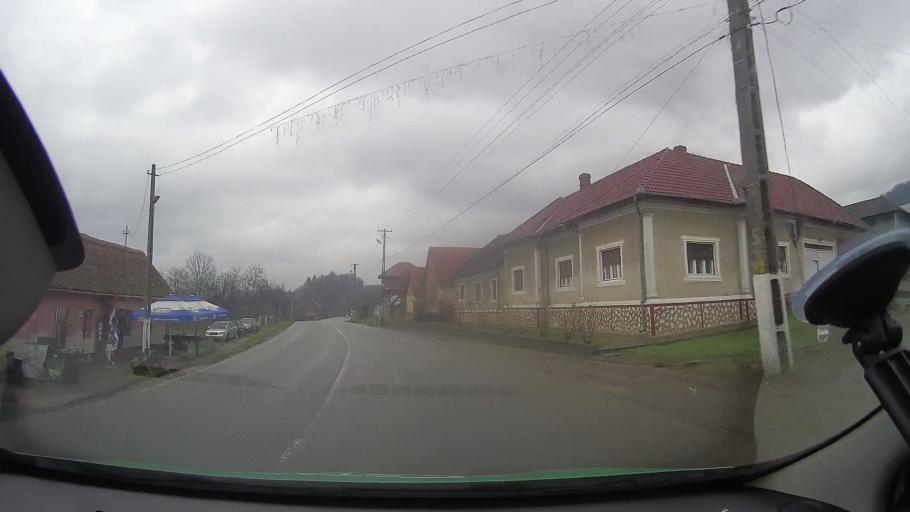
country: RO
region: Arad
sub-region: Comuna Almas
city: Almas
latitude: 46.2996
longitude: 22.1797
